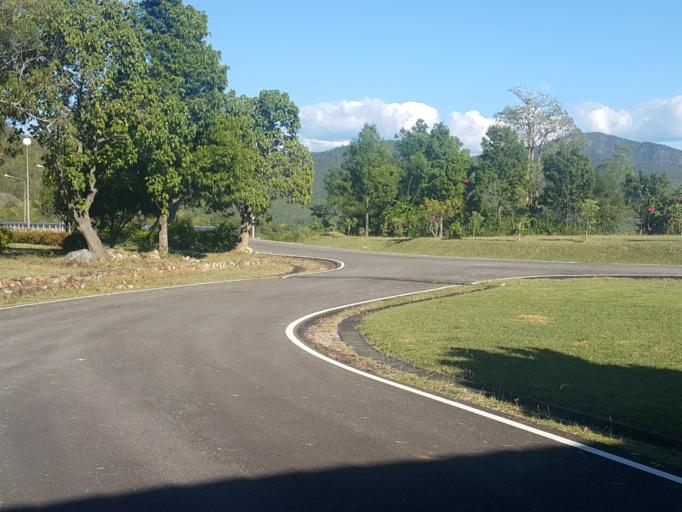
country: TH
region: Chiang Mai
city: San Sai
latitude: 18.9248
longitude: 99.1226
